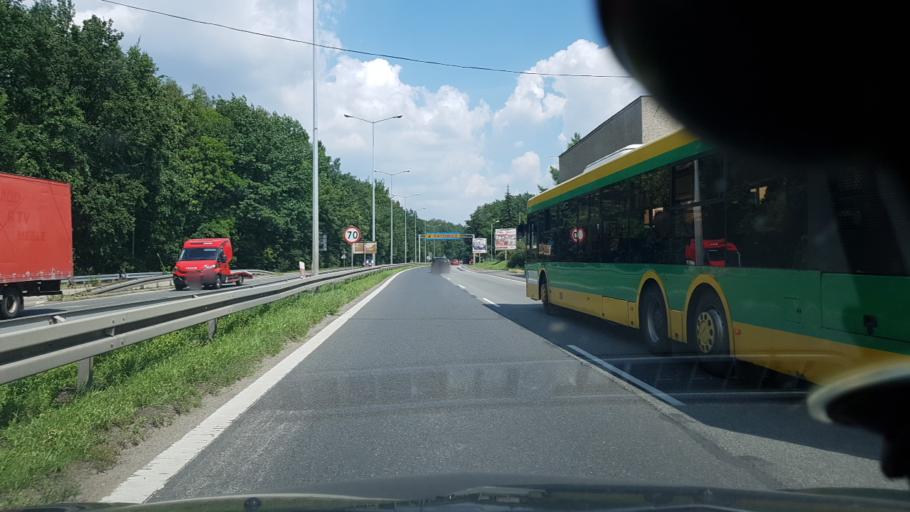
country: PL
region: Silesian Voivodeship
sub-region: Powiat mikolowski
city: Mikolow
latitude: 50.1966
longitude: 18.9326
